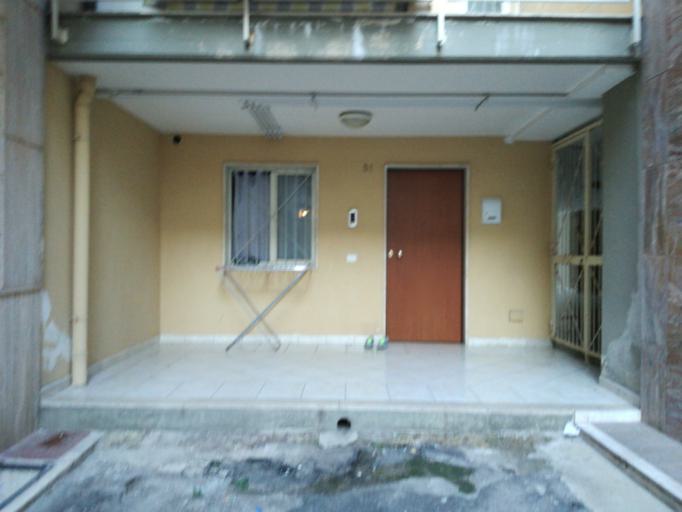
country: IT
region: Apulia
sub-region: Provincia di Bari
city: Triggiano
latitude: 41.0654
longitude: 16.9278
